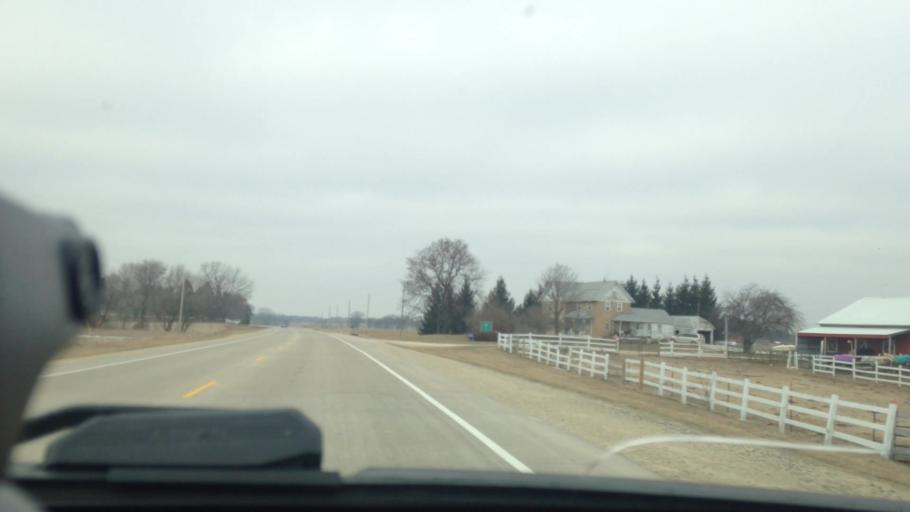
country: US
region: Wisconsin
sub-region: Dodge County
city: Horicon
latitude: 43.4689
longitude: -88.6740
